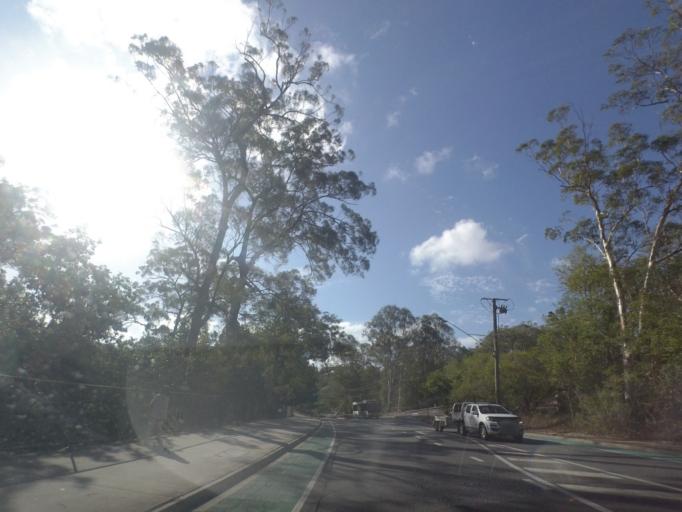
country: AU
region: Queensland
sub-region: Brisbane
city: Toowong
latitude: -27.4751
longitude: 152.9794
